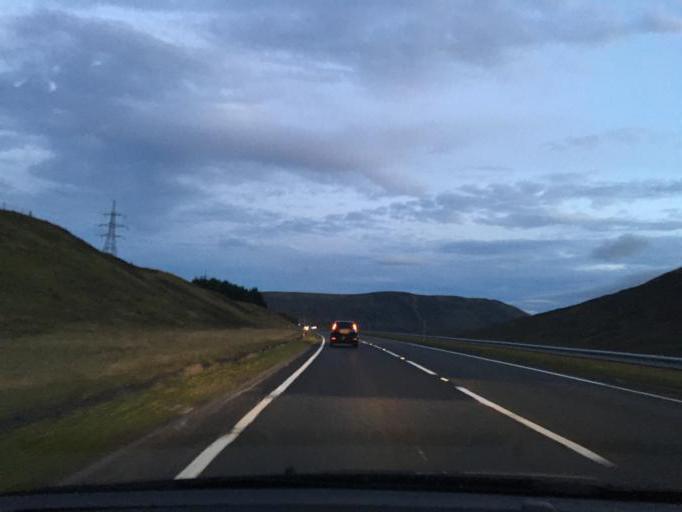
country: GB
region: Scotland
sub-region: Highland
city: Kingussie
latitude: 56.8505
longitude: -4.2437
